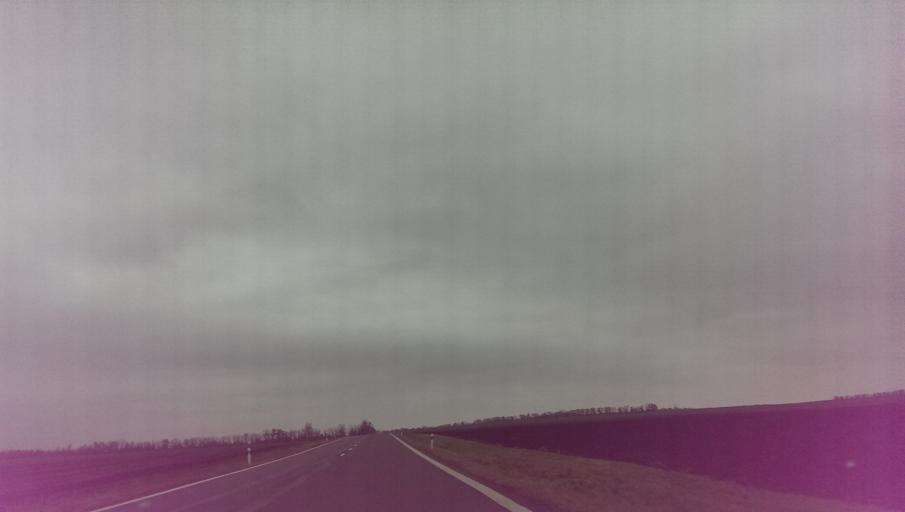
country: CZ
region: South Moravian
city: Miroslav
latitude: 48.9061
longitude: 16.3064
